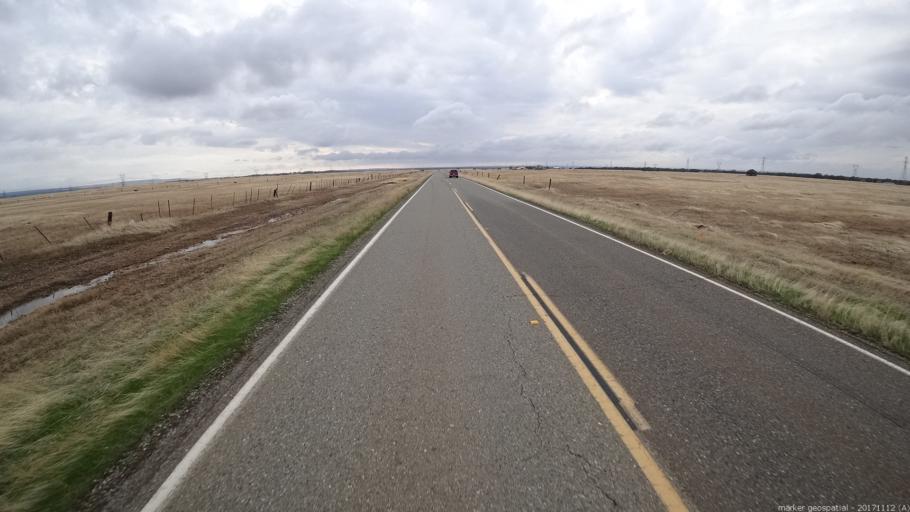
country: US
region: California
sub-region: Shasta County
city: Palo Cedro
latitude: 40.5221
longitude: -122.1786
